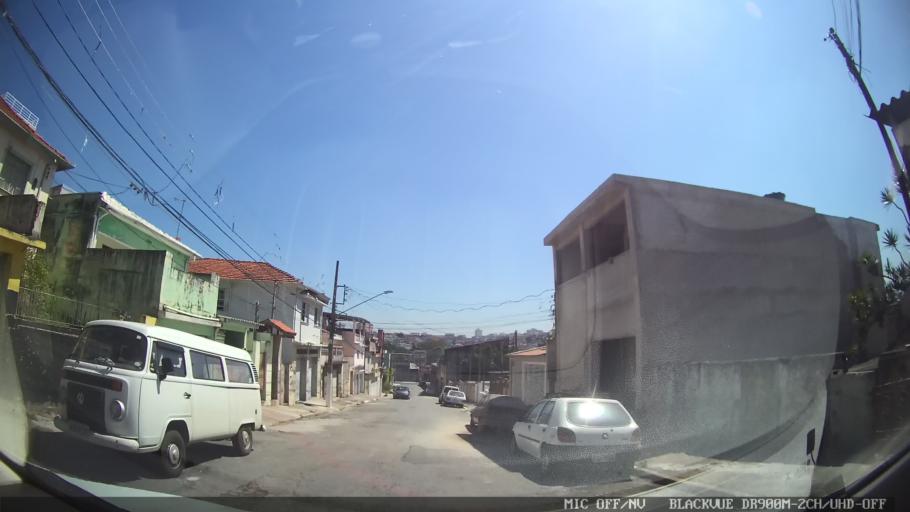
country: BR
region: Sao Paulo
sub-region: Sao Paulo
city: Sao Paulo
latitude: -23.4987
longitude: -46.6601
